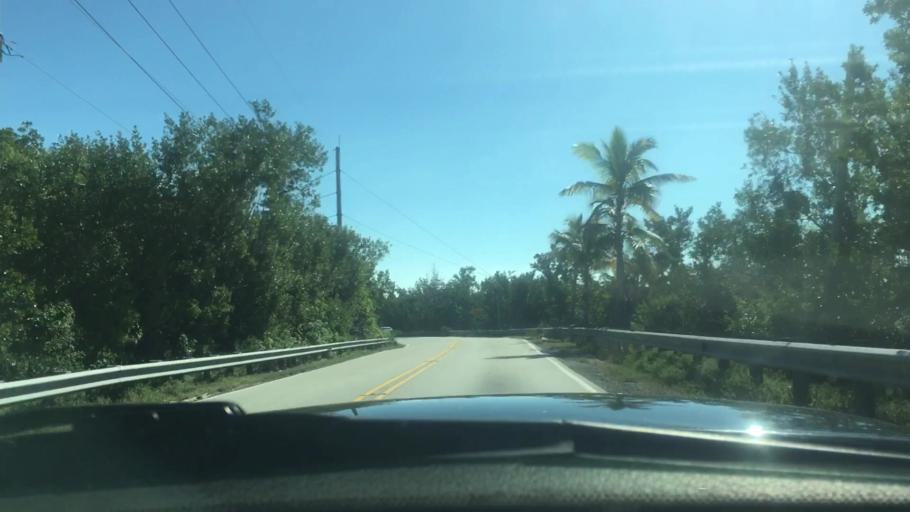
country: US
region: Florida
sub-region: Monroe County
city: North Key Largo
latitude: 25.2930
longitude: -80.3816
